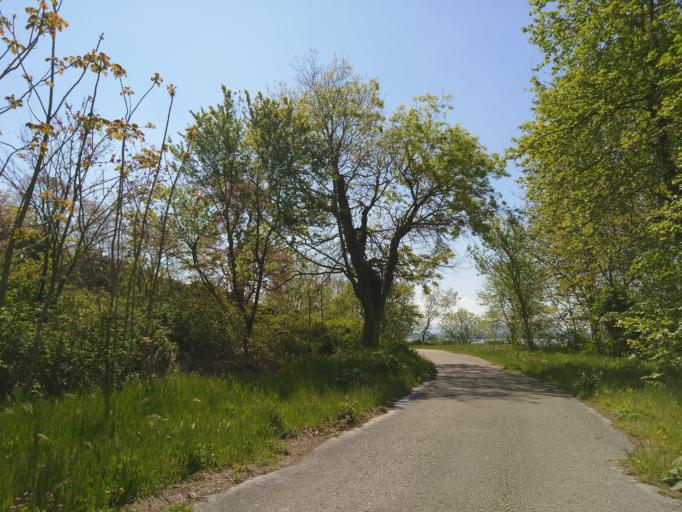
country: GR
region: Epirus
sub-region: Nomos Ioanninon
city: Ioannina
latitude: 39.6757
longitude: 20.8731
